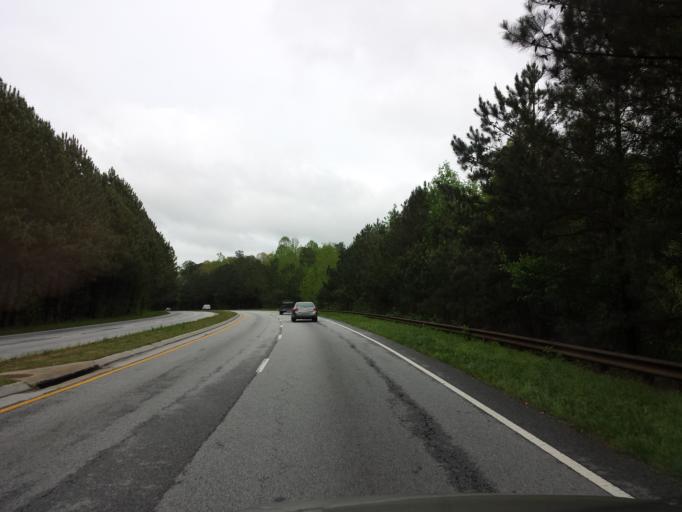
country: US
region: Georgia
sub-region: Cobb County
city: Mableton
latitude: 33.8459
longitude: -84.5480
